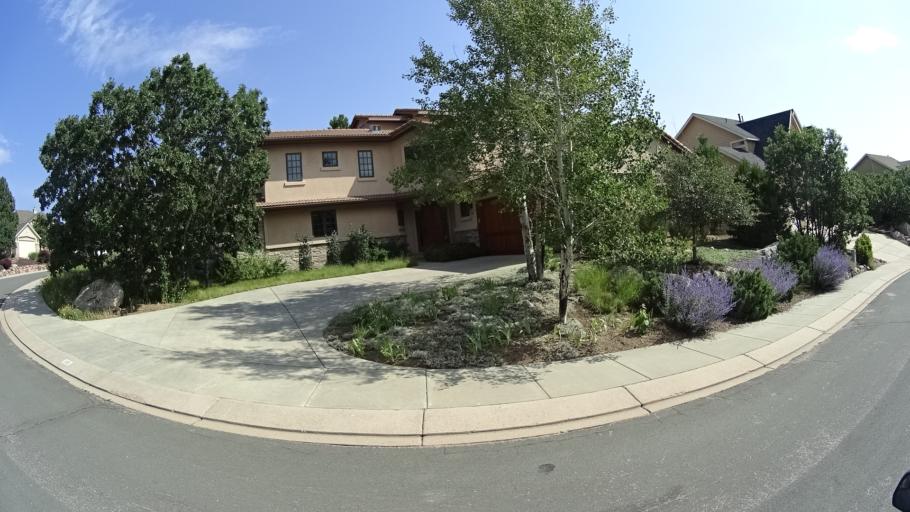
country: US
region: Colorado
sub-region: El Paso County
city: Fort Carson
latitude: 38.7509
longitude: -104.8360
